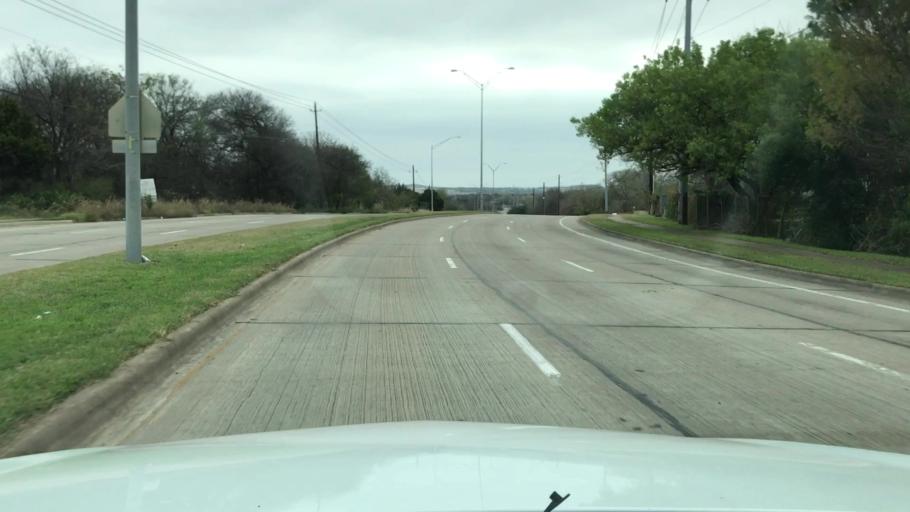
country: US
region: Texas
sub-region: Travis County
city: Onion Creek
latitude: 30.1857
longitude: -97.7574
